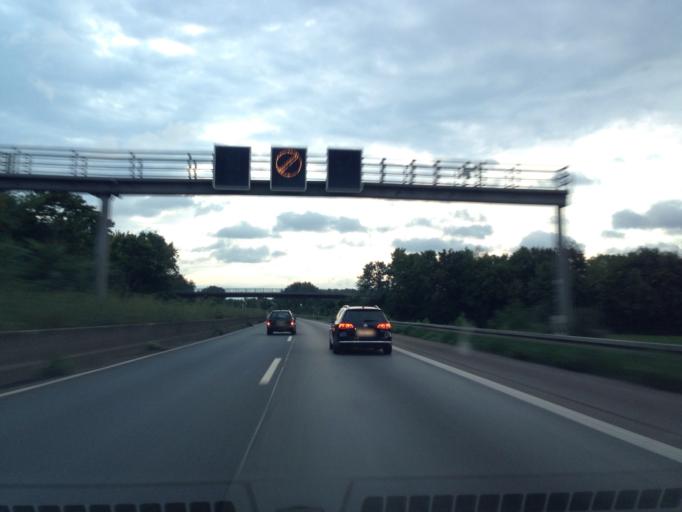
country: DE
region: North Rhine-Westphalia
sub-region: Regierungsbezirk Dusseldorf
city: Krefeld
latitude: 51.3769
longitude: 6.6215
